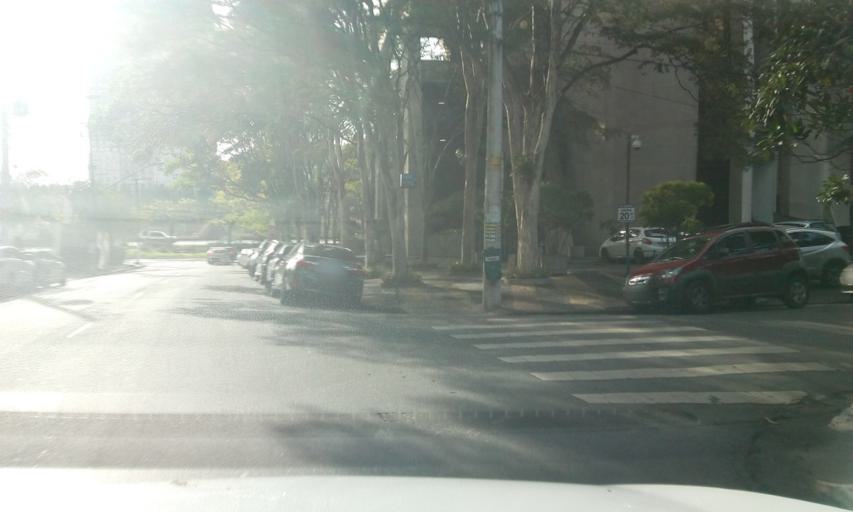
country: BR
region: Sao Paulo
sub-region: Sao Paulo
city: Sao Paulo
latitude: -23.6026
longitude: -46.6944
